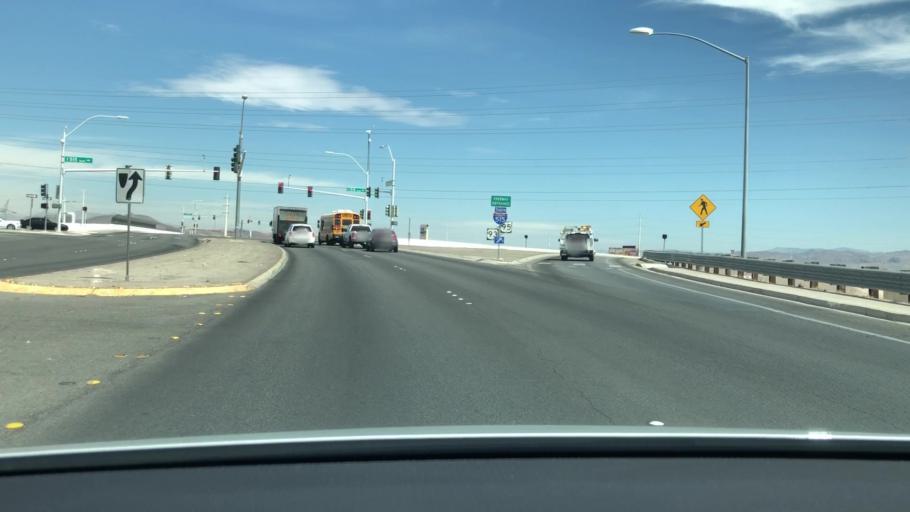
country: US
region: Nevada
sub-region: Clark County
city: Whitney
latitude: 36.0823
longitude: -115.0516
